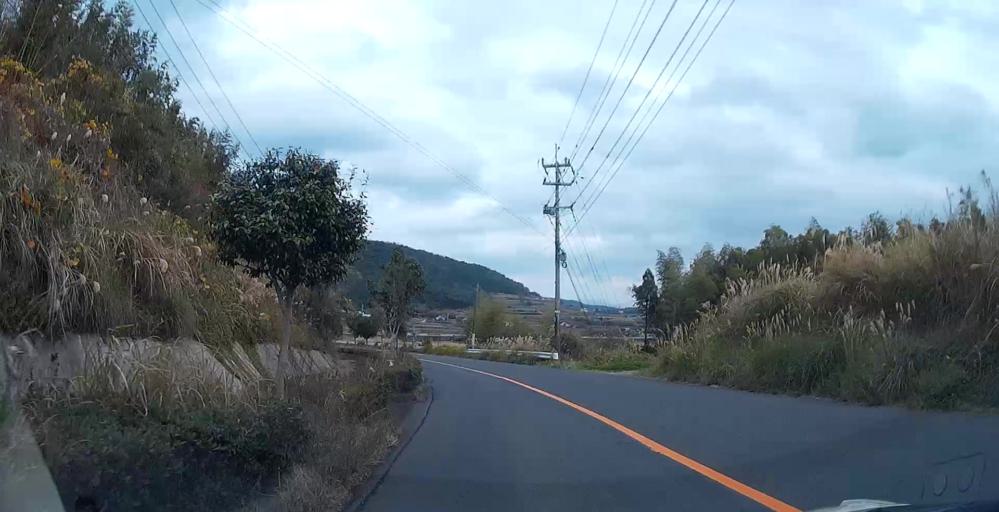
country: JP
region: Kagoshima
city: Akune
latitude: 32.0897
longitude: 130.1875
